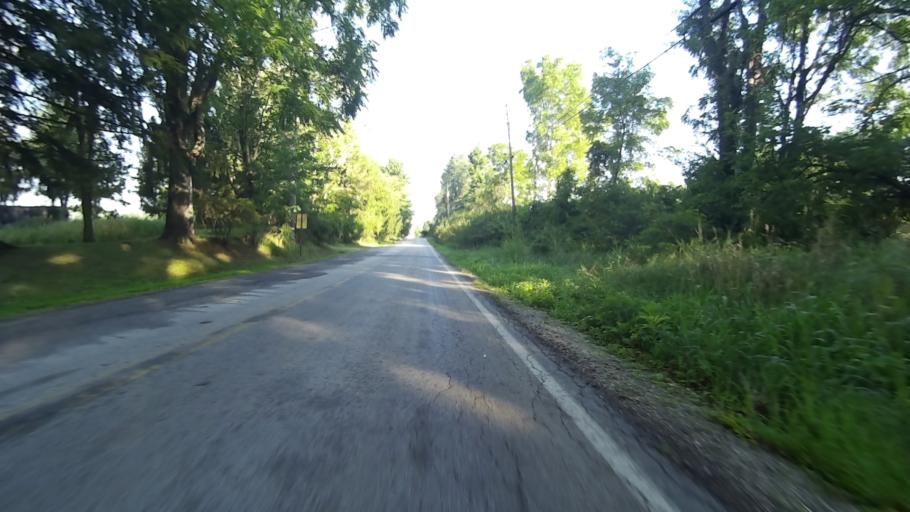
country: US
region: Ohio
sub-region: Portage County
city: Streetsboro
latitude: 41.2045
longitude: -81.3718
